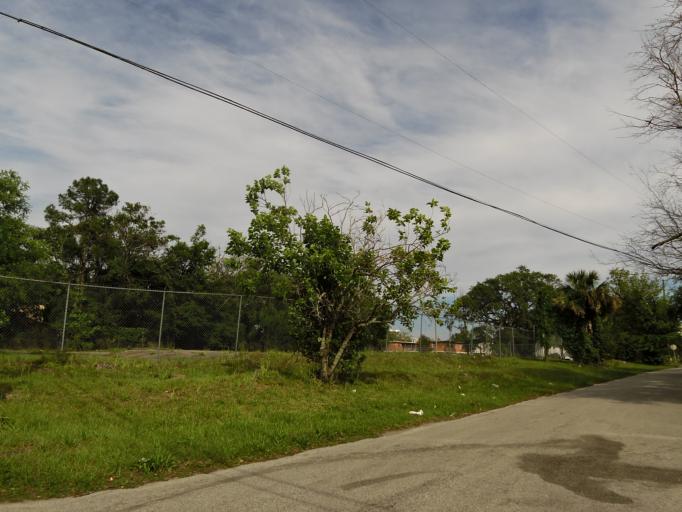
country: US
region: Florida
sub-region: Duval County
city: Jacksonville
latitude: 30.3255
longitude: -81.6764
